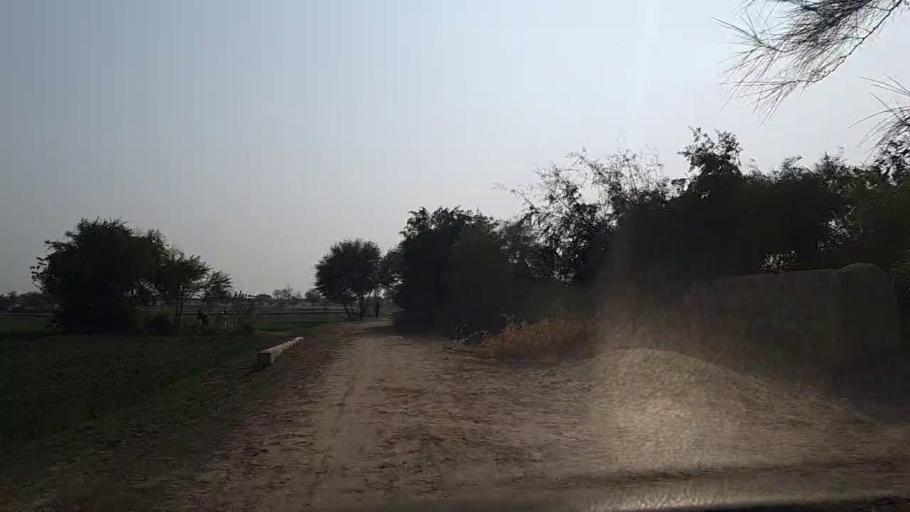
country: PK
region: Sindh
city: Daur
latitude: 26.4007
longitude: 68.4200
